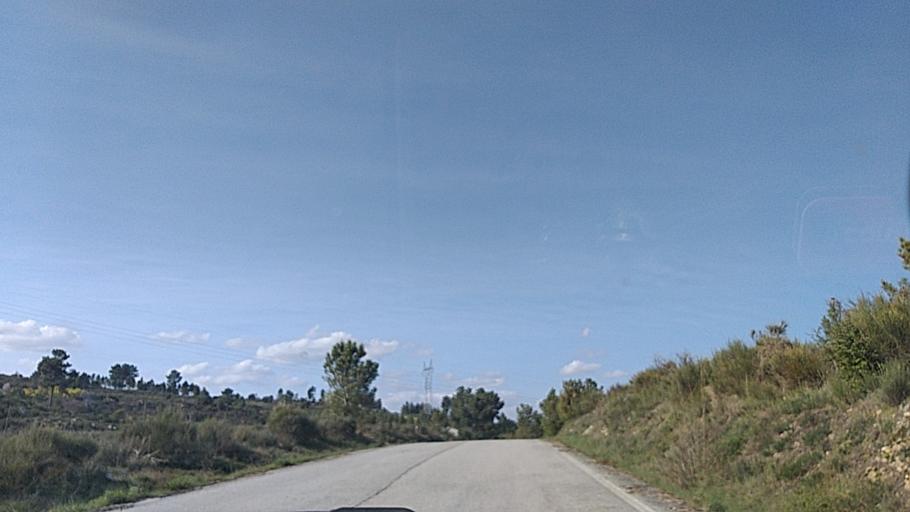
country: PT
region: Guarda
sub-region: Celorico da Beira
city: Celorico da Beira
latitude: 40.6514
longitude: -7.3970
